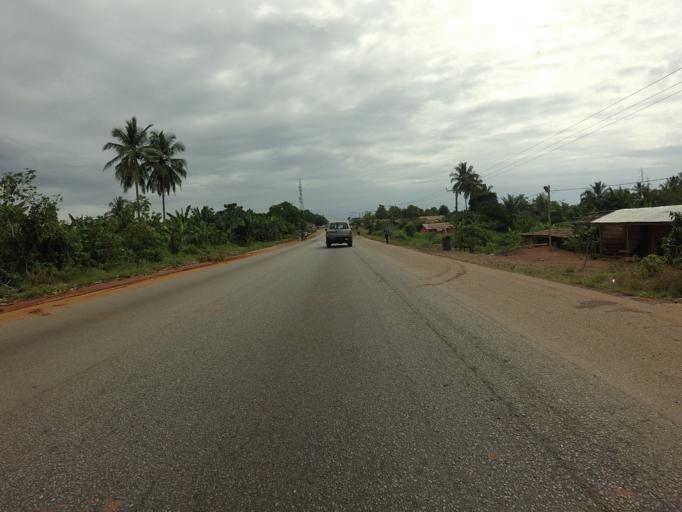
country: GH
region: Eastern
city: Nkawkaw
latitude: 6.5993
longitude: -0.8919
